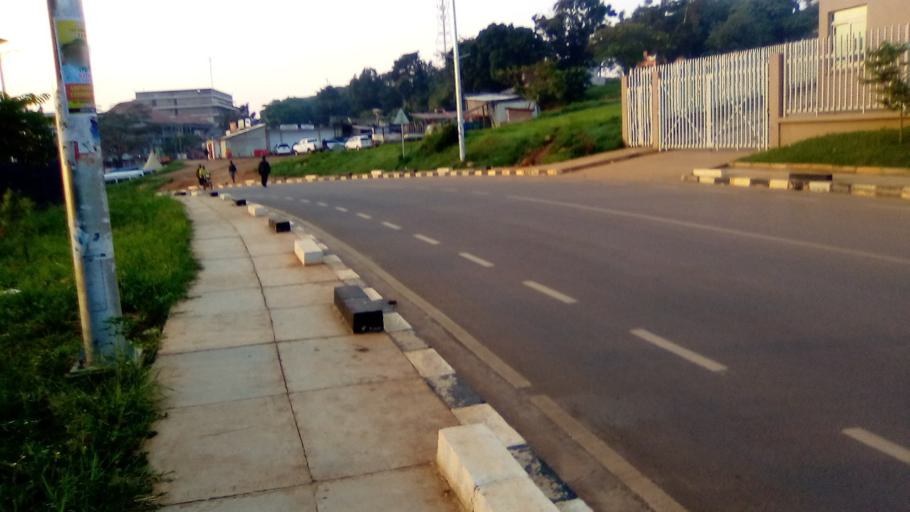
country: UG
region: Central Region
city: Masaka
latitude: -0.3393
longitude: 31.7375
